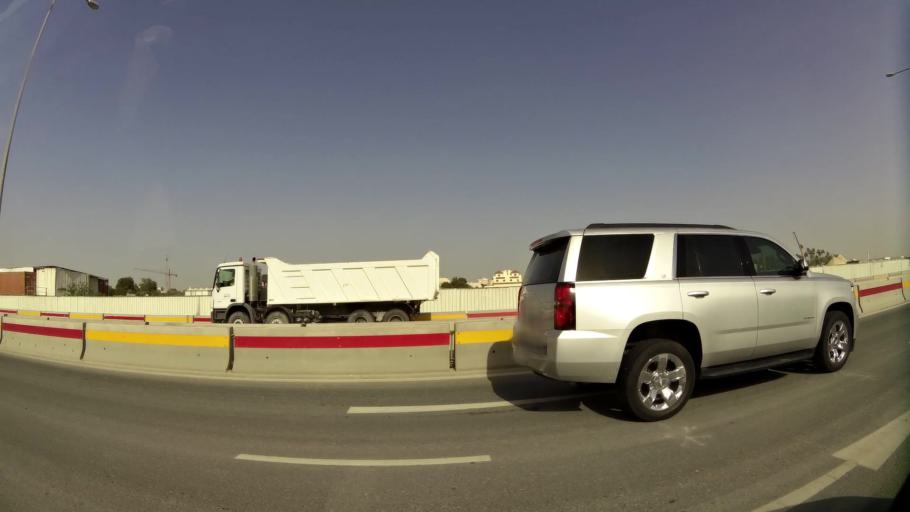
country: QA
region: Baladiyat ar Rayyan
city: Ar Rayyan
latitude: 25.3236
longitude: 51.4481
